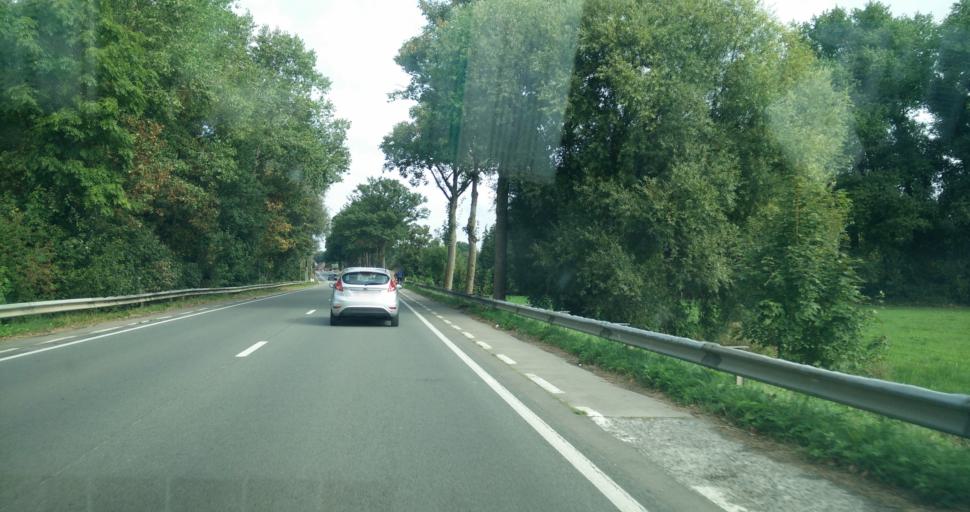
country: BE
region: Flanders
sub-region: Provincie Oost-Vlaanderen
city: Ronse
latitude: 50.7278
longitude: 3.5872
